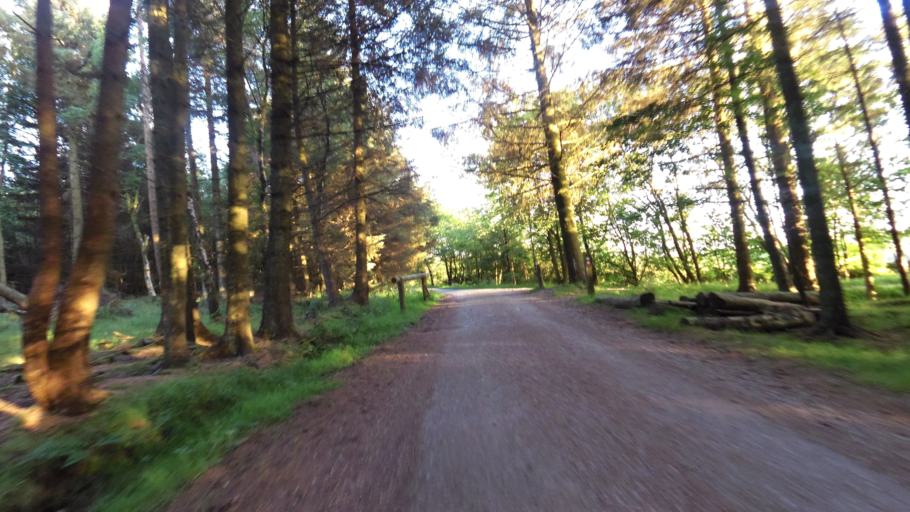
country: GB
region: England
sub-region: North Yorkshire
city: Settle
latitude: 54.0113
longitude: -2.3798
